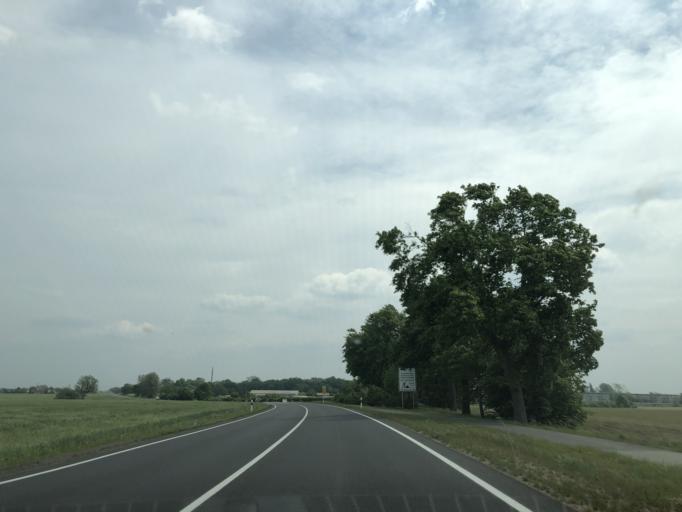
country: DE
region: Brandenburg
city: Kyritz
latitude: 52.9537
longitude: 12.3708
